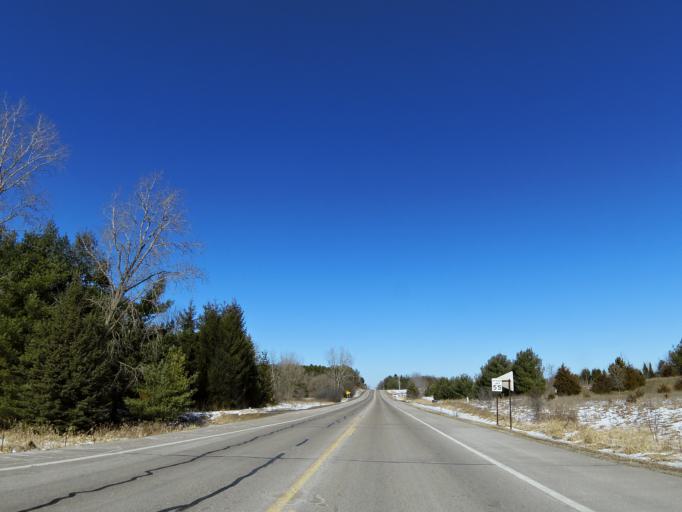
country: US
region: Minnesota
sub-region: Washington County
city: Lake Elmo
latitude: 45.0223
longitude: -92.8833
